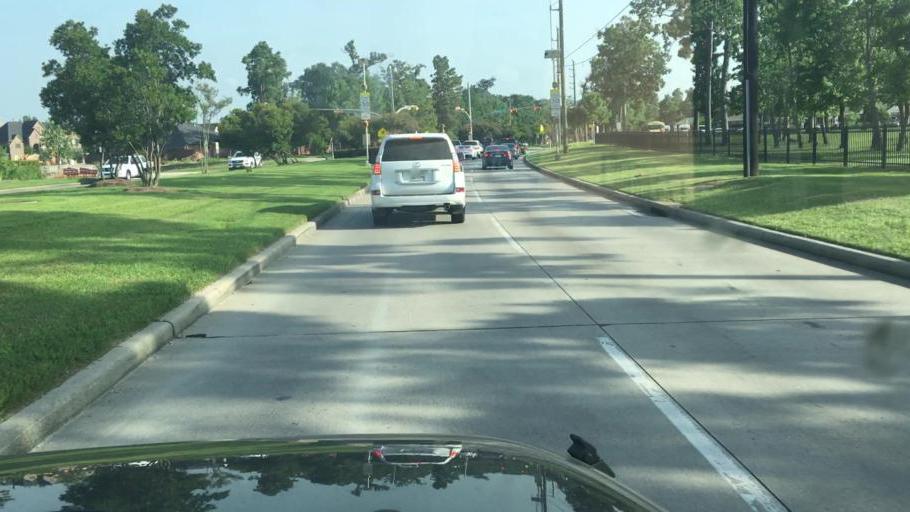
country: US
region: Texas
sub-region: Harris County
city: Atascocita
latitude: 29.9627
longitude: -95.1688
